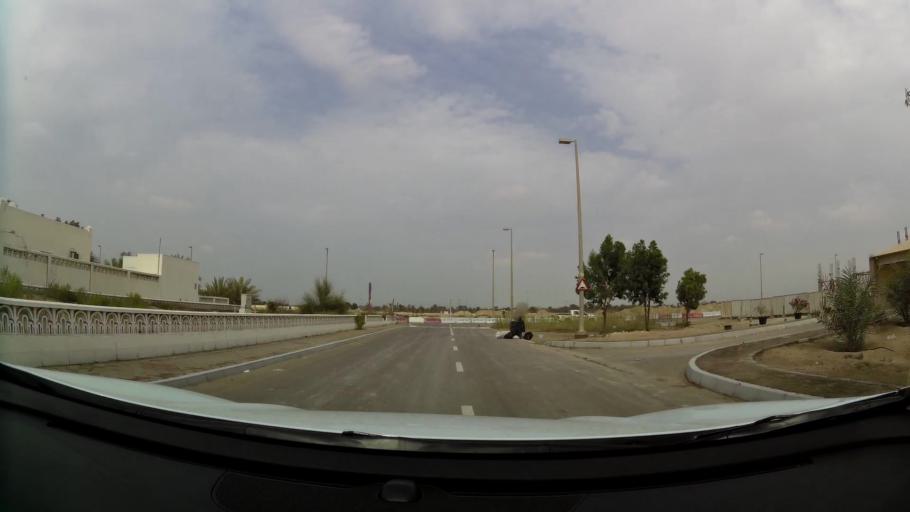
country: AE
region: Abu Dhabi
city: Abu Dhabi
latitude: 24.6368
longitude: 54.7183
